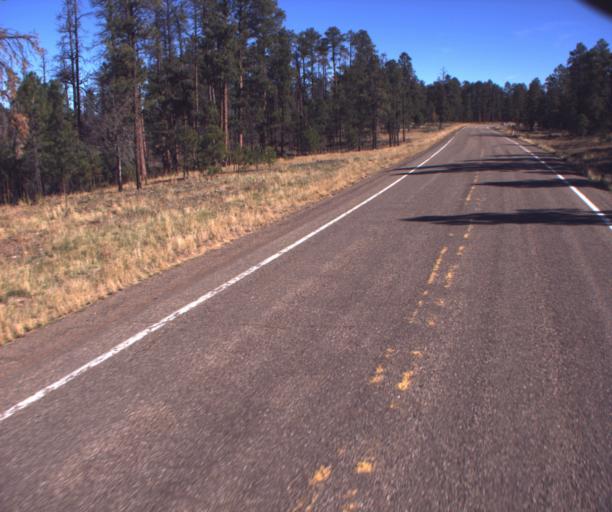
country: US
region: Arizona
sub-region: Coconino County
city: Fredonia
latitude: 36.7353
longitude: -112.2212
